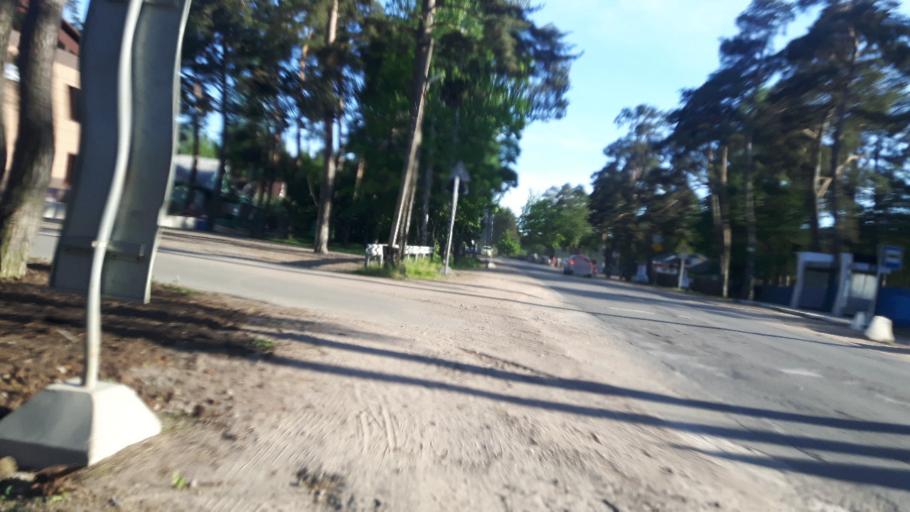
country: RU
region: Leningrad
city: Vistino
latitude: 59.7709
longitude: 28.4743
